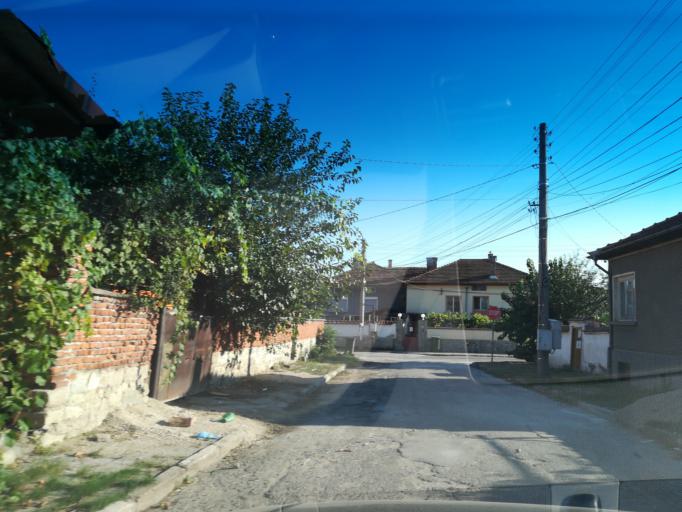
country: BG
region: Stara Zagora
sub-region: Obshtina Chirpan
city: Chirpan
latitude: 42.1051
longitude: 25.2195
